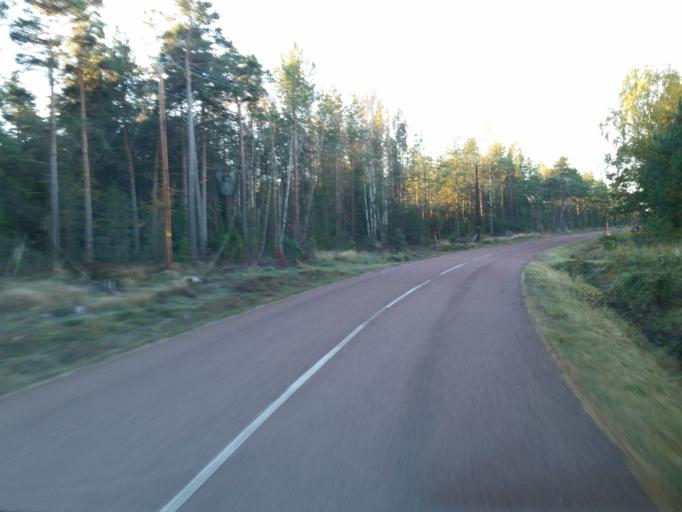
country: AX
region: Alands skaergard
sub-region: Vardoe
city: Vardoe
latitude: 60.3044
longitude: 20.3835
